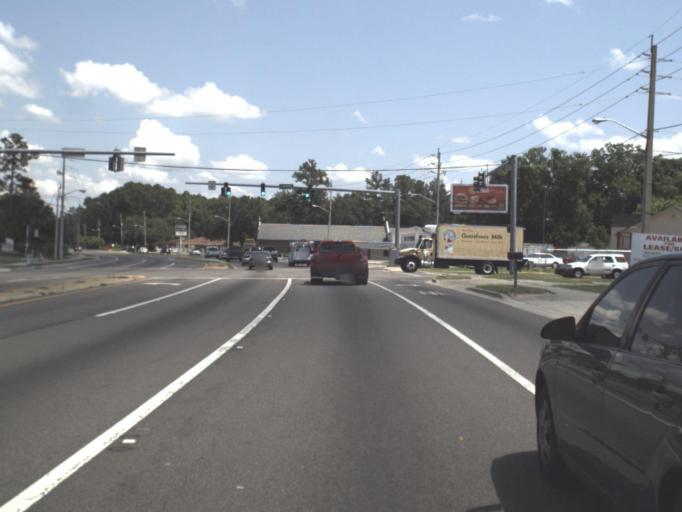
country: US
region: Florida
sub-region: Duval County
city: Jacksonville
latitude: 30.4292
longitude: -81.6940
